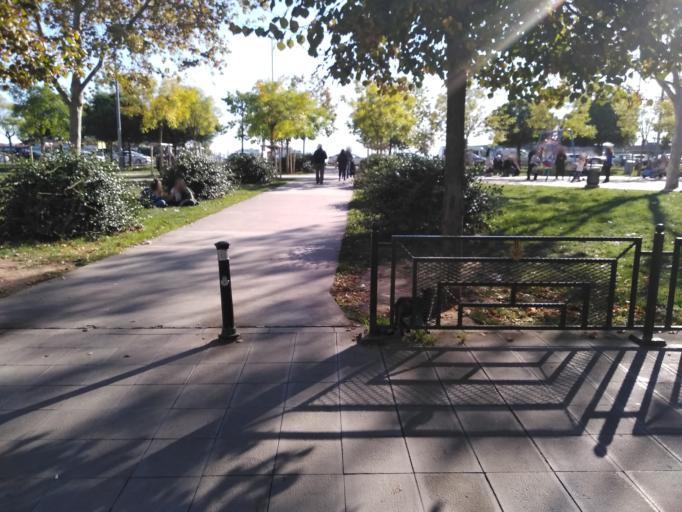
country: TR
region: Istanbul
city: Maltepe
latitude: 40.8882
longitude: 29.1885
